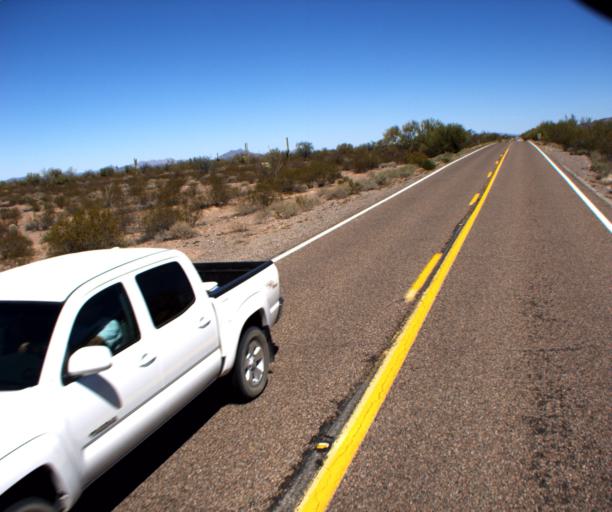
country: US
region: Arizona
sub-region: Pima County
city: Ajo
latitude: 32.1405
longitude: -112.7664
